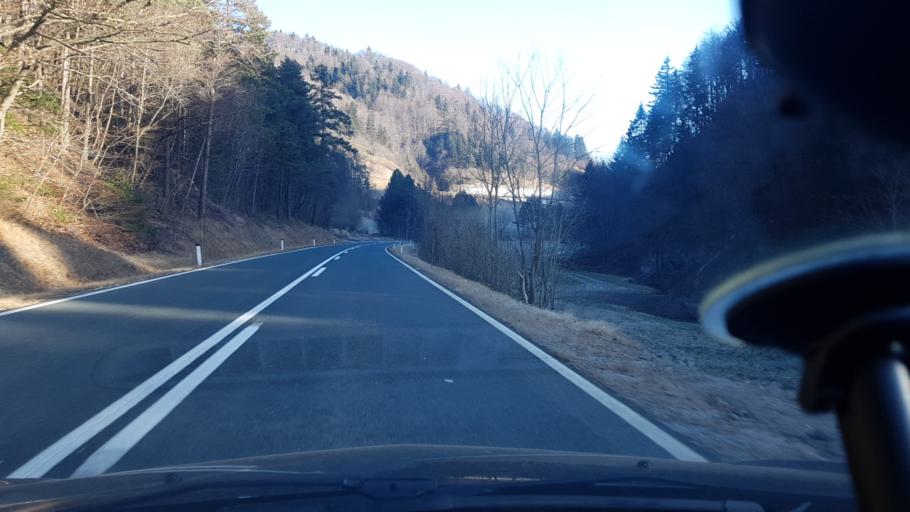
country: SI
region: Zagorje ob Savi
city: Izlake
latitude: 46.1778
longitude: 14.8458
